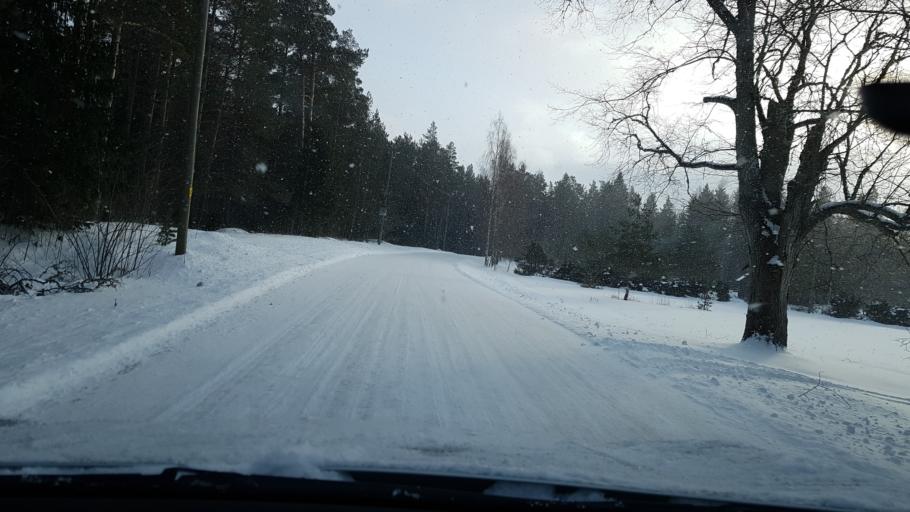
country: EE
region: Harju
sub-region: Nissi vald
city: Turba
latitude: 59.1872
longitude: 24.1398
